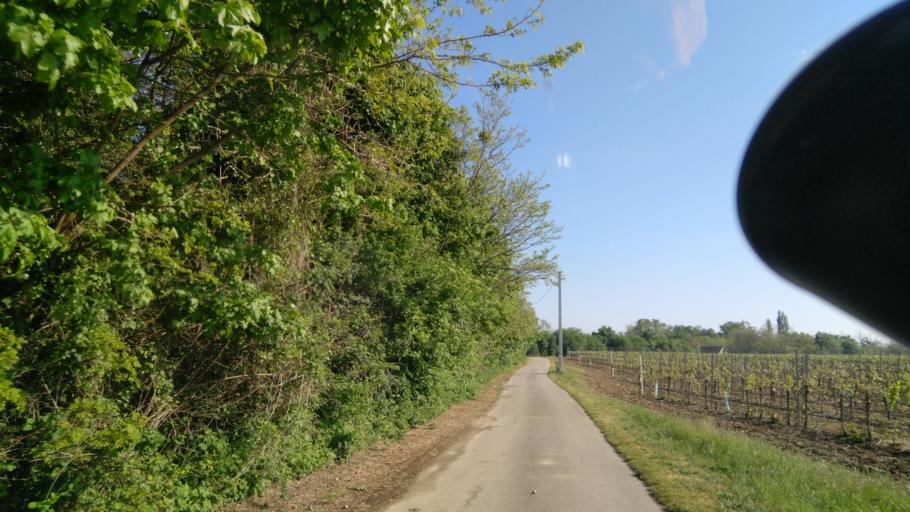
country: HU
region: Zala
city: Sarmellek
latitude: 46.7547
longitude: 17.1415
